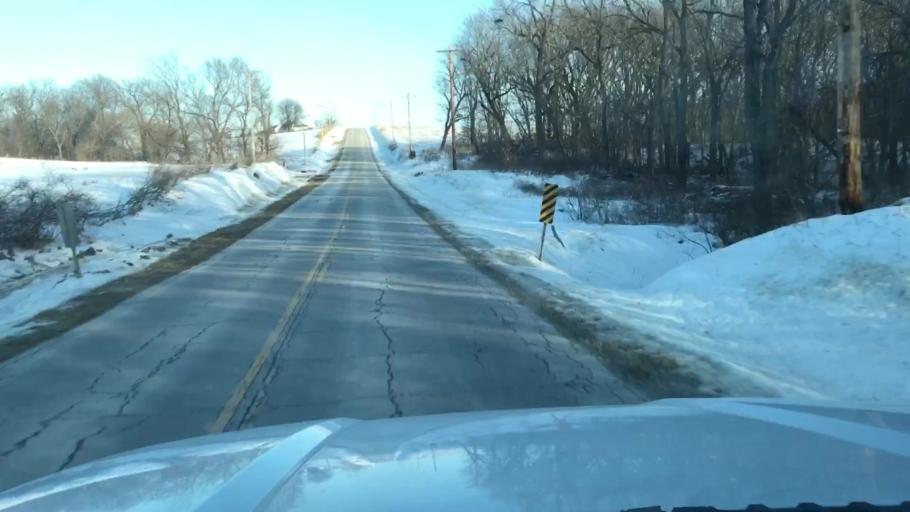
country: US
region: Missouri
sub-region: Andrew County
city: Savannah
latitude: 40.0247
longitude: -94.8917
